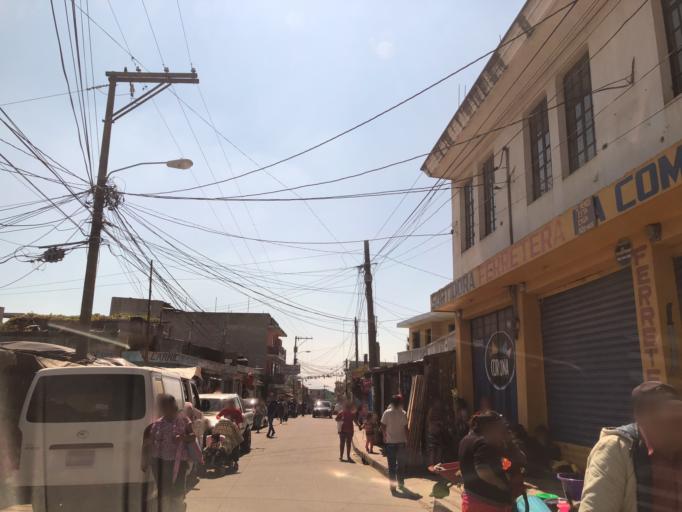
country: GT
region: Guatemala
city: Mixco
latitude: 14.6209
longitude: -90.5820
